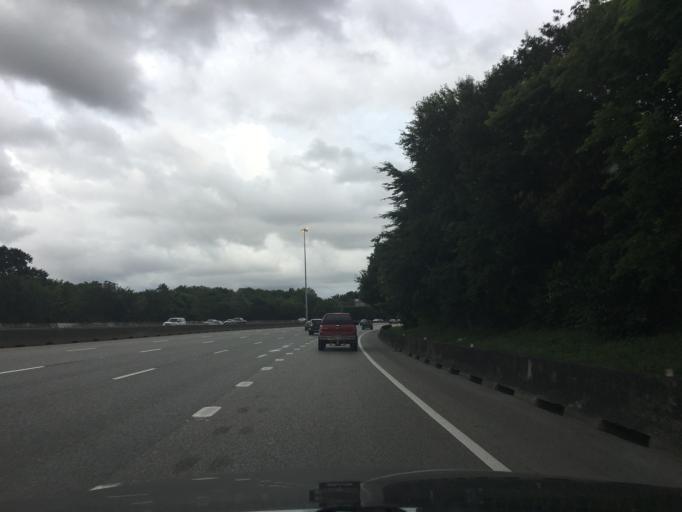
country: US
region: Texas
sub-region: Harris County
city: Houston
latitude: 29.7845
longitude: -95.3699
